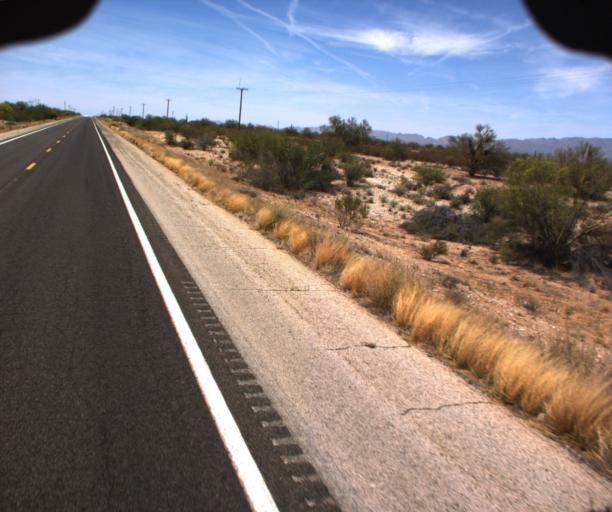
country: US
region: Arizona
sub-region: La Paz County
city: Salome
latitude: 33.9120
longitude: -113.2724
